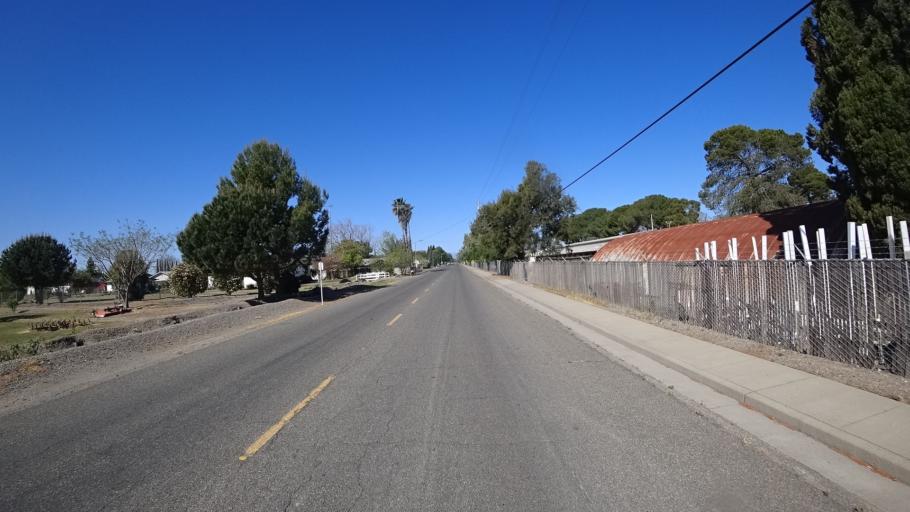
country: US
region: California
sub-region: Glenn County
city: Orland
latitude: 39.7401
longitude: -122.1796
